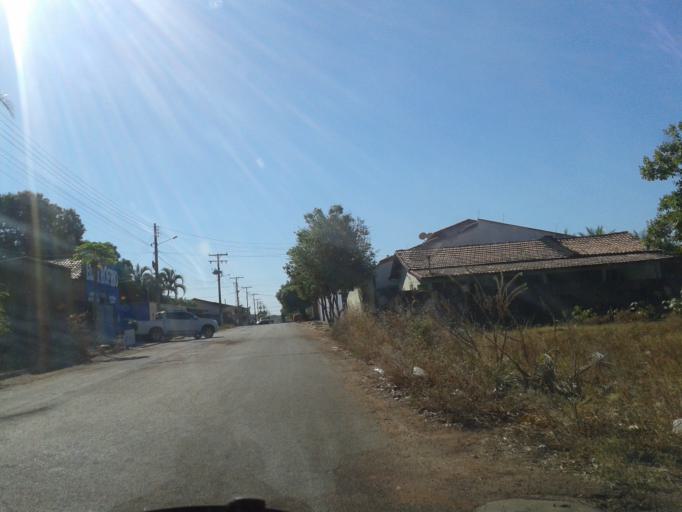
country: BR
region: Goias
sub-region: Sao Miguel Do Araguaia
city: Sao Miguel do Araguaia
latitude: -13.2783
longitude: -50.1569
